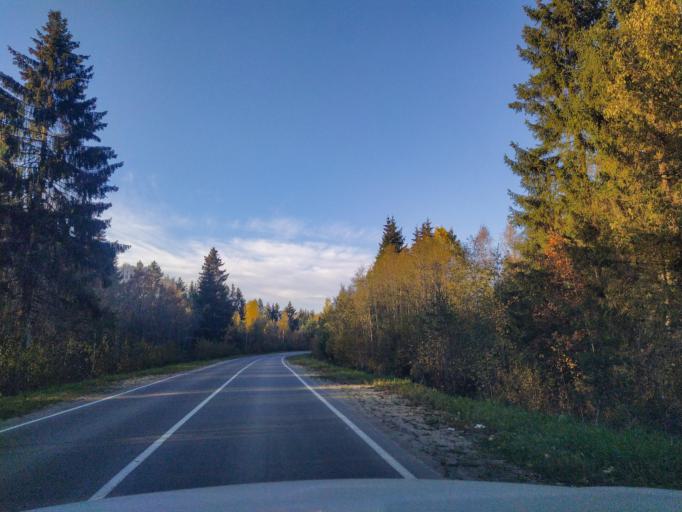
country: RU
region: Leningrad
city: Siverskiy
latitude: 59.3071
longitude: 30.0306
